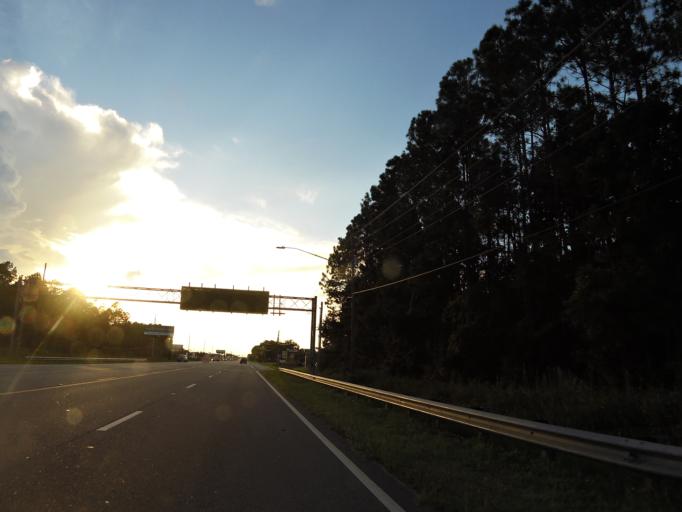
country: US
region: Georgia
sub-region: Camden County
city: Kingsland
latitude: 30.7822
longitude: -81.6316
